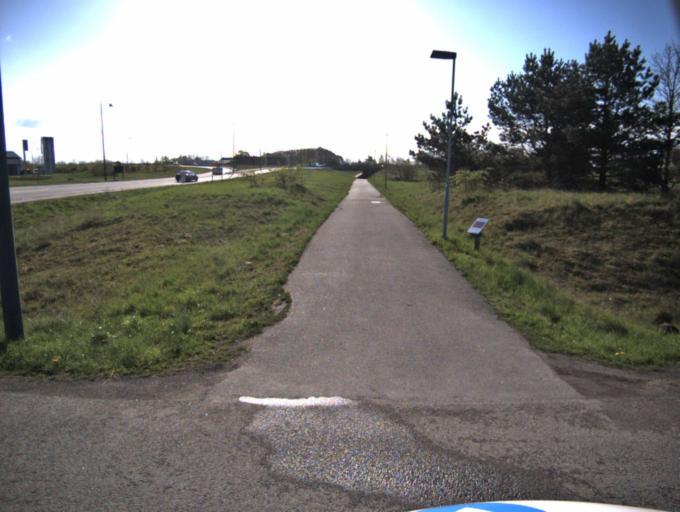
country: SE
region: Skane
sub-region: Kristianstads Kommun
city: Norra Asum
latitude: 56.0022
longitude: 14.0986
